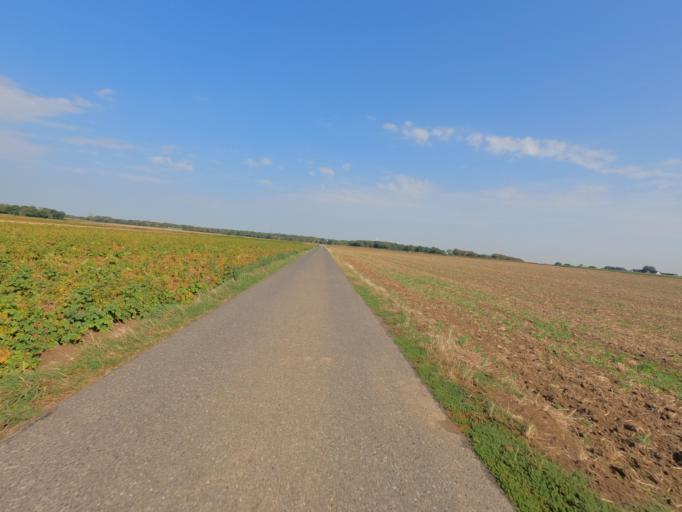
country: DE
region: North Rhine-Westphalia
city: Huckelhoven
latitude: 51.0975
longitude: 6.2321
